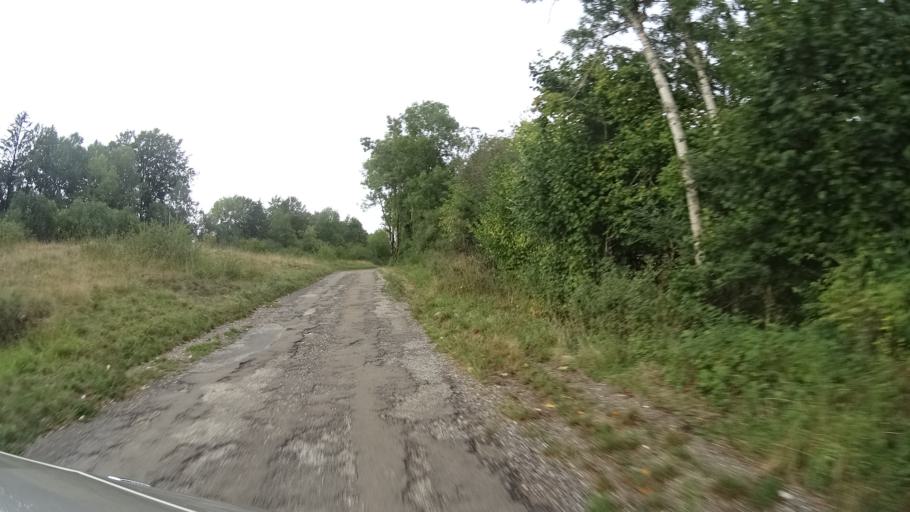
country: FR
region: Franche-Comte
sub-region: Departement du Jura
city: Morbier
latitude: 46.6175
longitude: 5.9675
